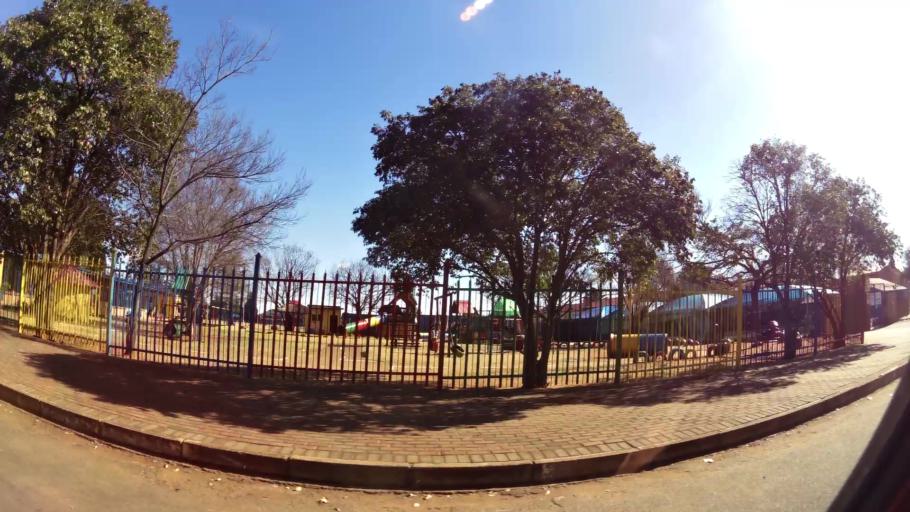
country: ZA
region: Gauteng
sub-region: West Rand District Municipality
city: Carletonville
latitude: -26.3541
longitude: 27.3893
